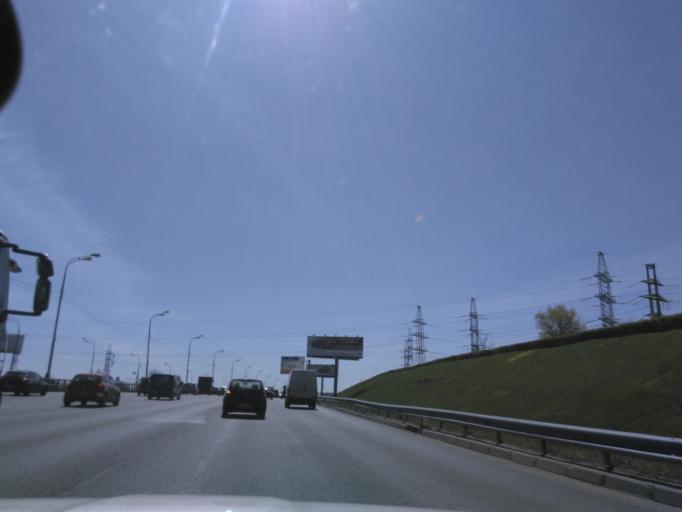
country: RU
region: Moscow
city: Strogino
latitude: 55.8394
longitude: 37.3951
